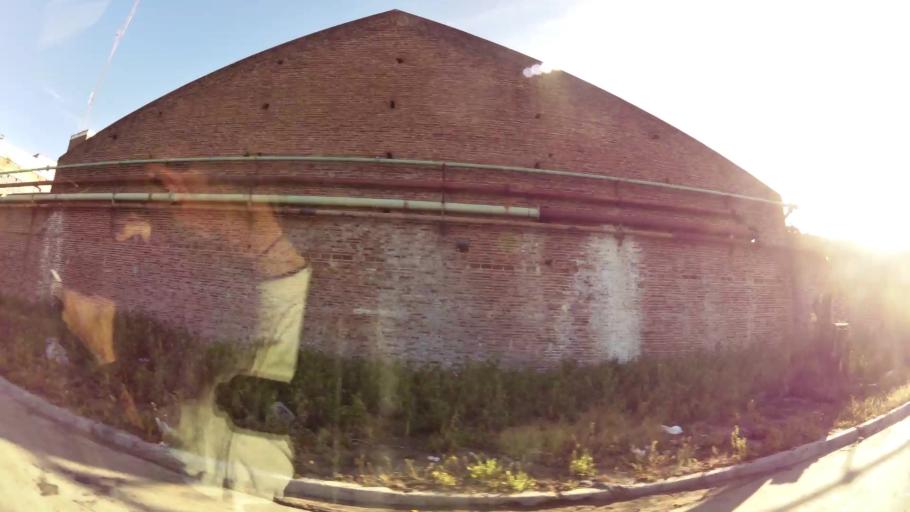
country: AR
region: Buenos Aires
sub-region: Partido de Quilmes
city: Quilmes
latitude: -34.8129
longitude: -58.2020
